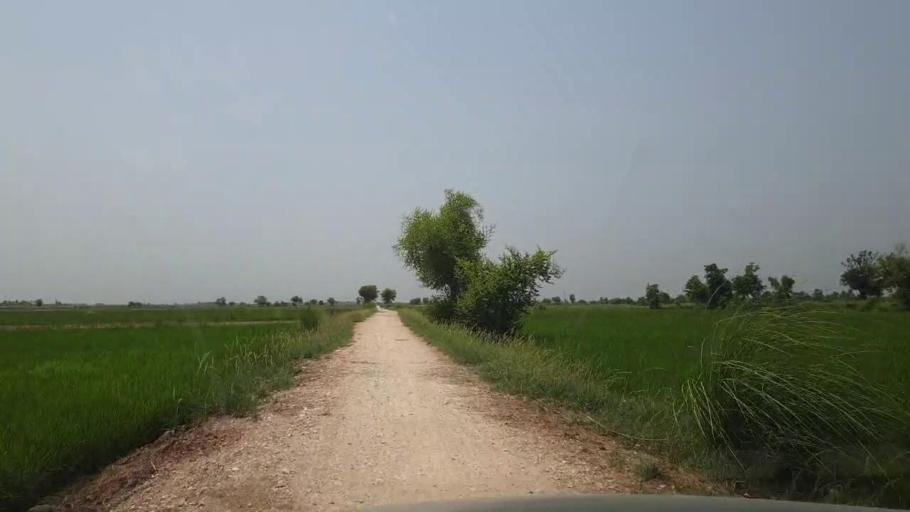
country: PK
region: Sindh
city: Garhi Yasin
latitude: 27.8669
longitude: 68.4862
